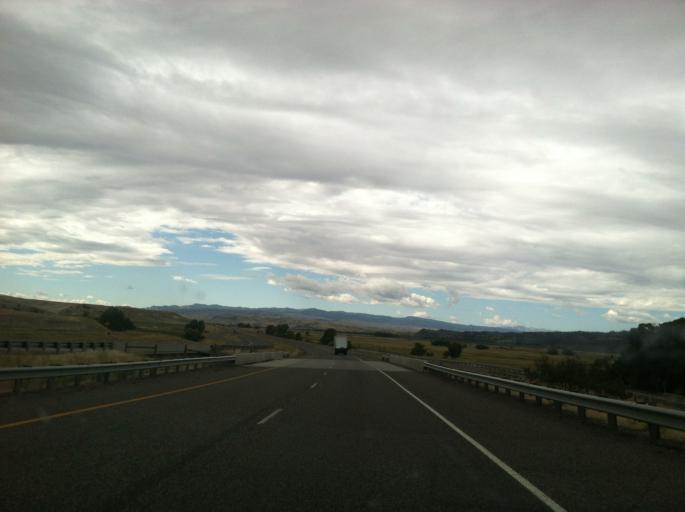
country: US
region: Montana
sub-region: Park County
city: Livingston
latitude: 45.7135
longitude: -110.4004
